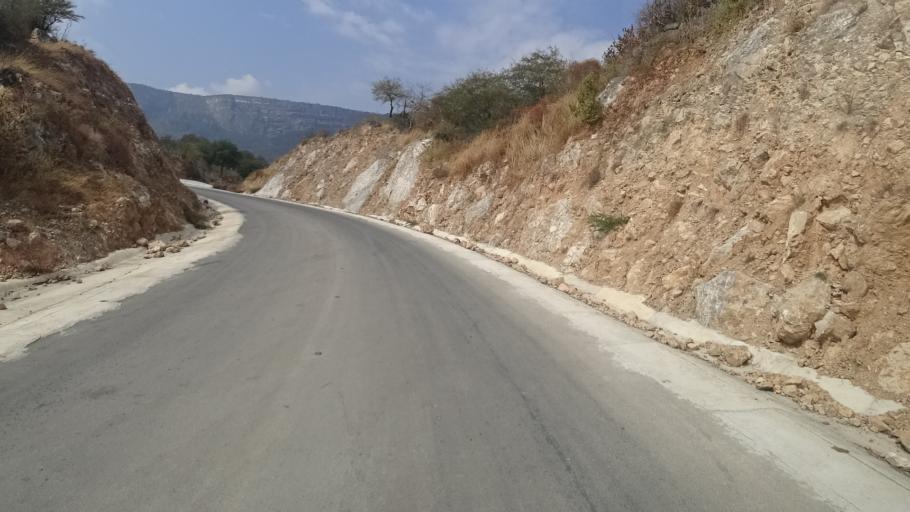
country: YE
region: Al Mahrah
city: Hawf
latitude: 16.7094
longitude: 53.2592
